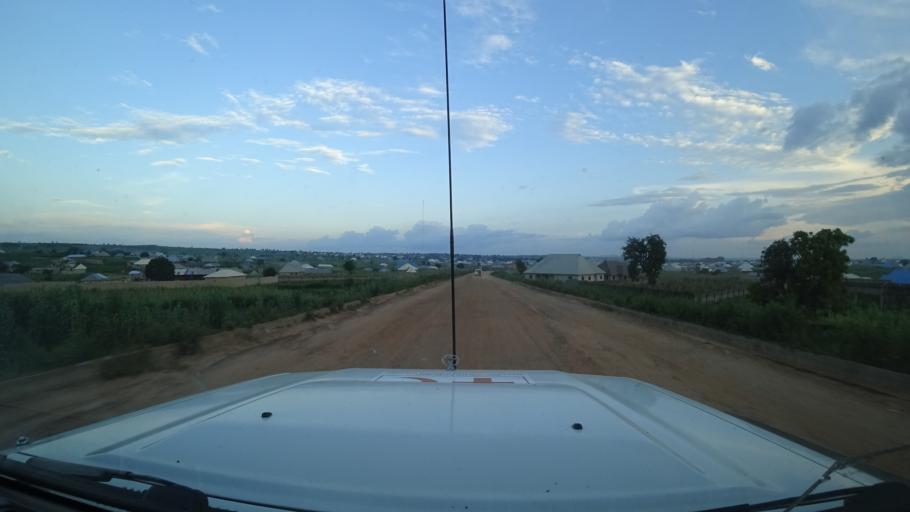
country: NG
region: Niger
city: Minna
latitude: 9.6500
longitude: 6.5792
